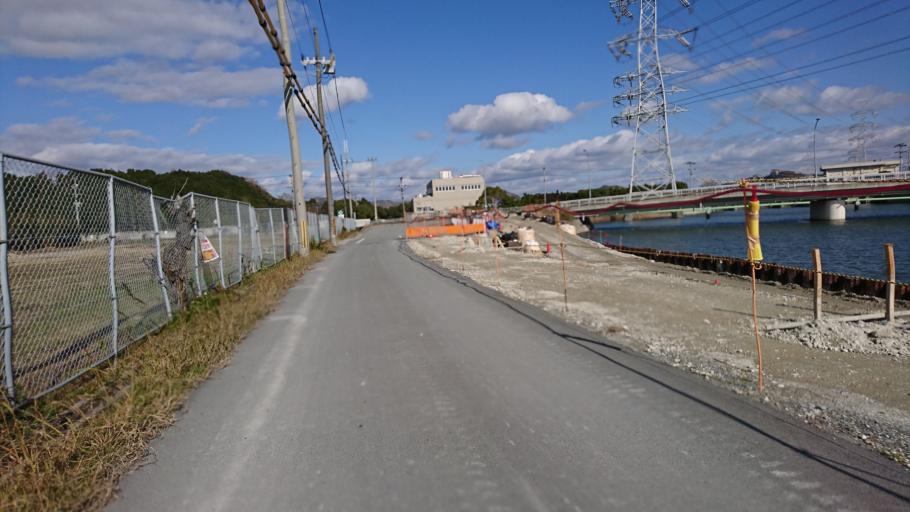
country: JP
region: Hyogo
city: Shirahamacho-usazakiminami
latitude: 34.7675
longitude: 134.7683
